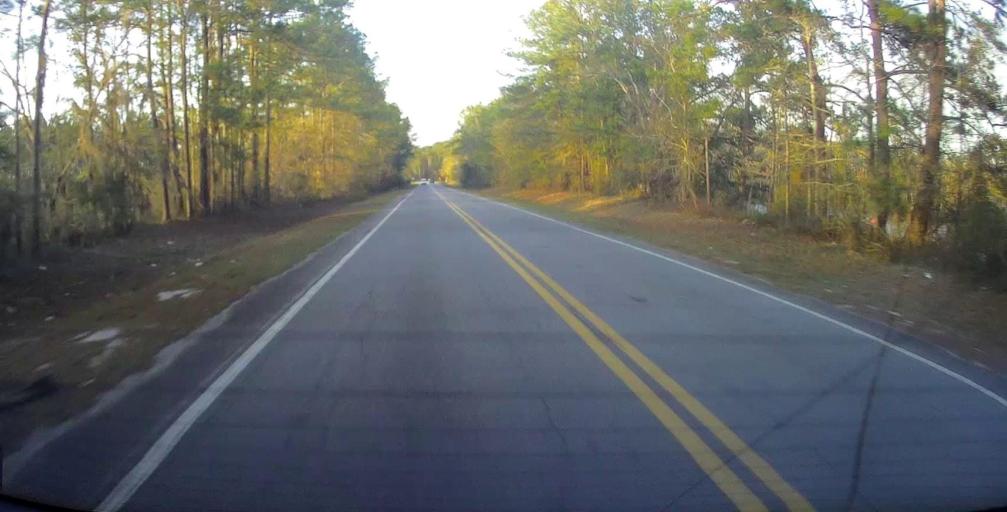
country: US
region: Georgia
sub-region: Chatham County
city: Bloomingdale
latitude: 32.1607
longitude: -81.3860
